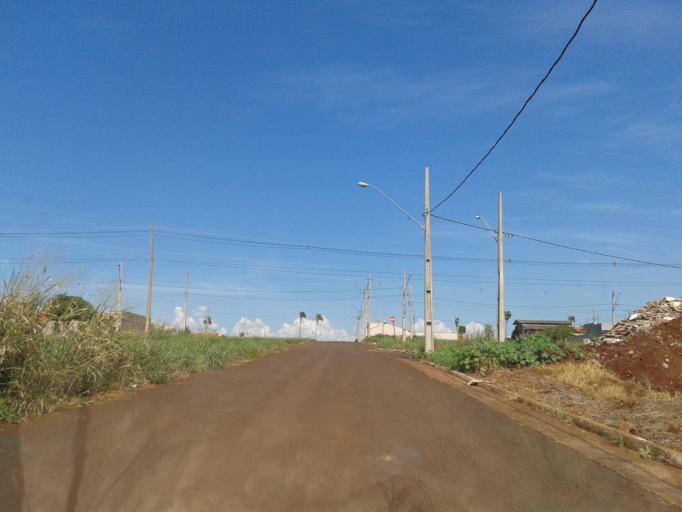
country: BR
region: Goias
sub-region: Itumbiara
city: Itumbiara
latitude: -18.4265
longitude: -49.1840
